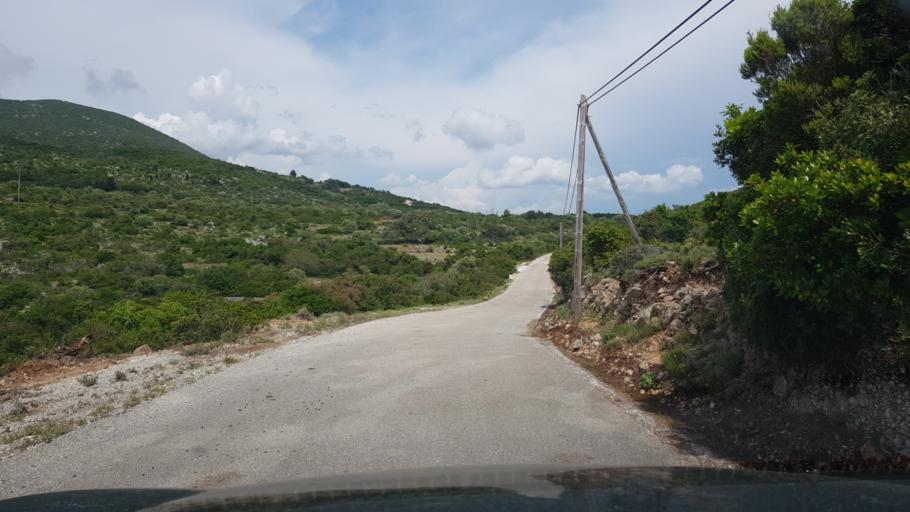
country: GR
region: Ionian Islands
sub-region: Lefkada
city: Nidri
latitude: 38.6079
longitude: 20.5632
